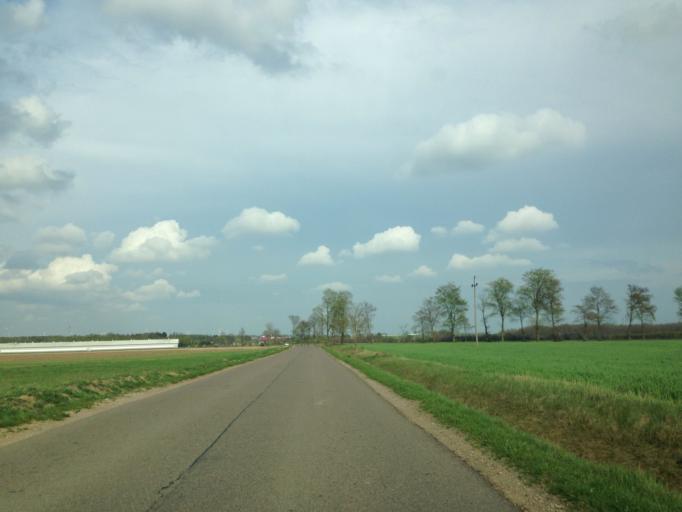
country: PL
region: Masovian Voivodeship
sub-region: Powiat zurominski
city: Lubowidz
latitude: 53.0678
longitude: 19.8513
